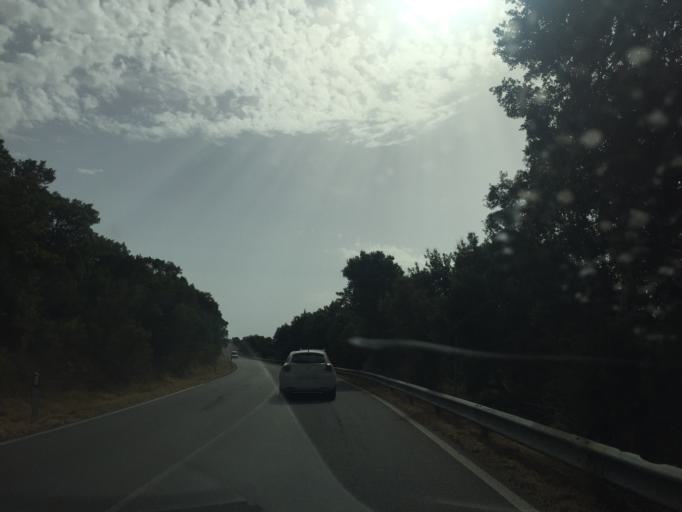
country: IT
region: Sardinia
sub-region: Provincia di Olbia-Tempio
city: Sant'Antonio di Gallura
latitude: 40.9789
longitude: 9.2574
